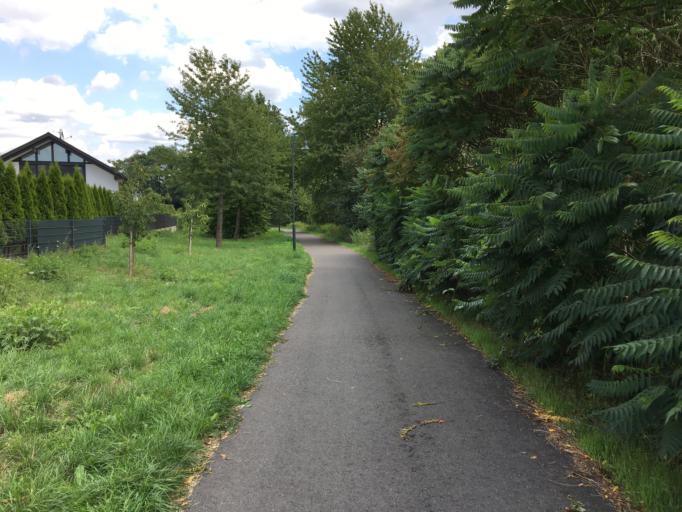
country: DE
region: North Rhine-Westphalia
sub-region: Regierungsbezirk Koln
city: Rosrath
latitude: 50.8963
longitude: 7.1774
